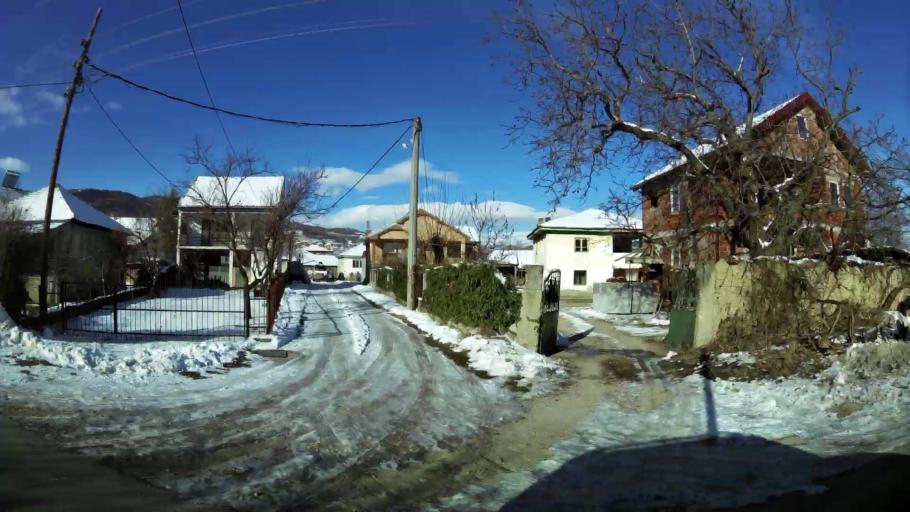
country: MK
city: Grchec
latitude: 41.9756
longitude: 21.3114
